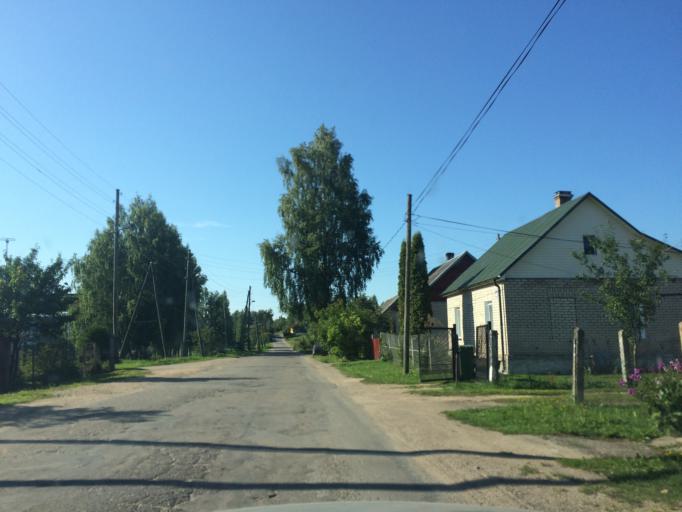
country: LV
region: Rezekne
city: Rezekne
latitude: 56.4894
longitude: 27.3349
